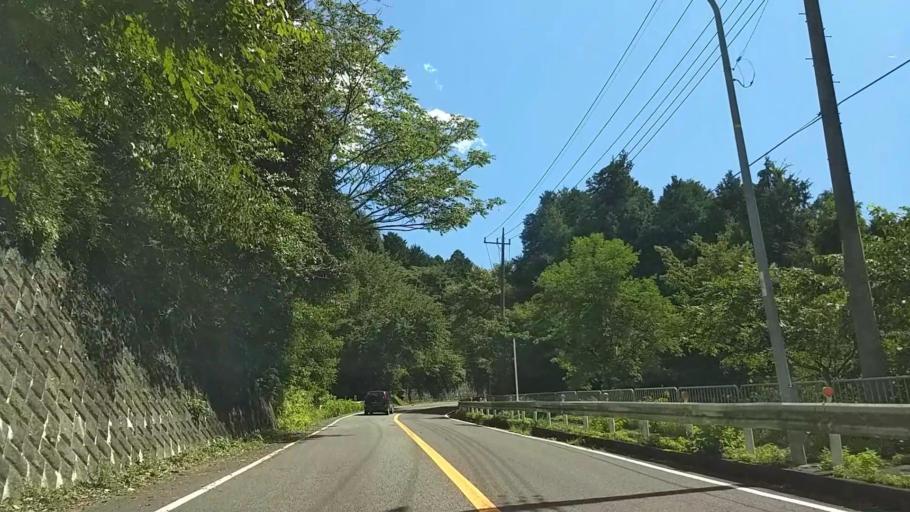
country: JP
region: Tokyo
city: Hachioji
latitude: 35.5591
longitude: 139.2821
